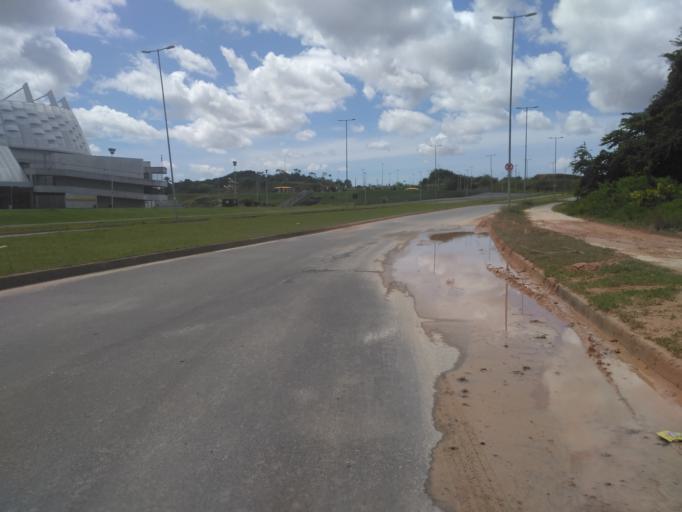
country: BR
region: Pernambuco
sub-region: Sao Lourenco Da Mata
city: Sao Lourenco da Mata
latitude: -8.0432
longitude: -35.0088
